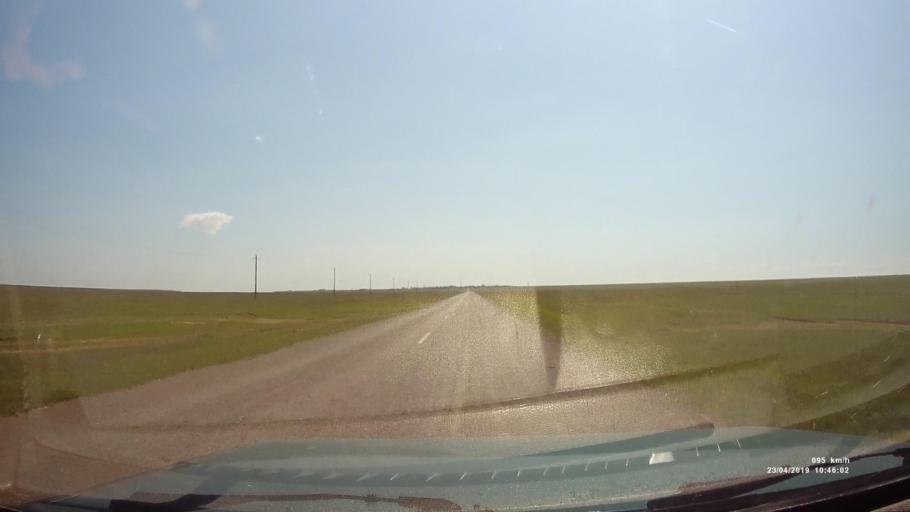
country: RU
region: Kalmykiya
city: Yashalta
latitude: 46.4462
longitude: 42.6845
